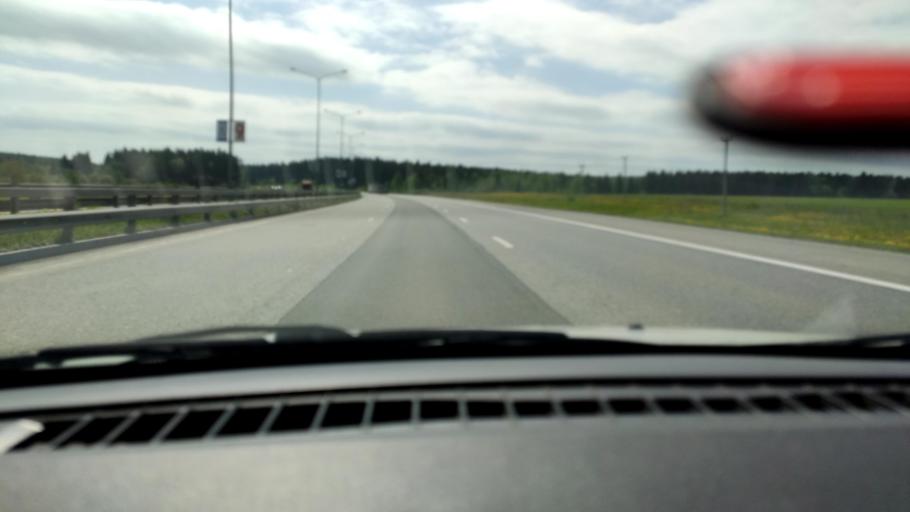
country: RU
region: Perm
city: Lobanovo
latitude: 57.8655
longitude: 56.2594
